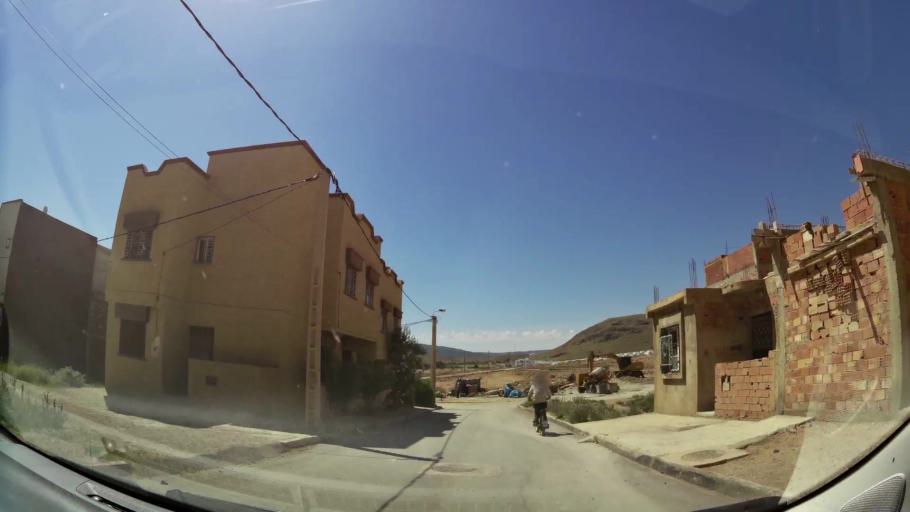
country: MA
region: Oriental
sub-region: Oujda-Angad
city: Oujda
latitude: 34.6513
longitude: -1.8677
